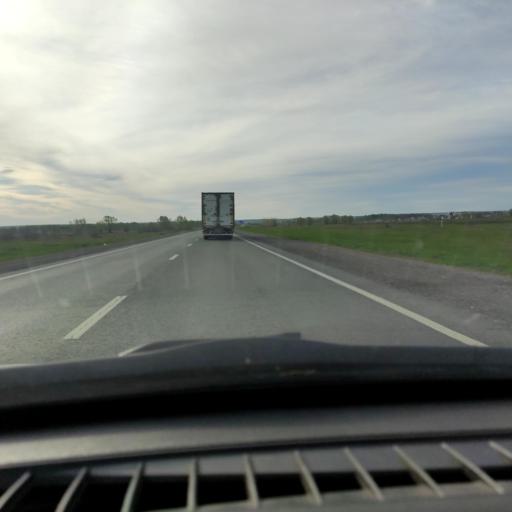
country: RU
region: Samara
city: Krasnyy Yar
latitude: 53.5122
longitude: 50.4148
